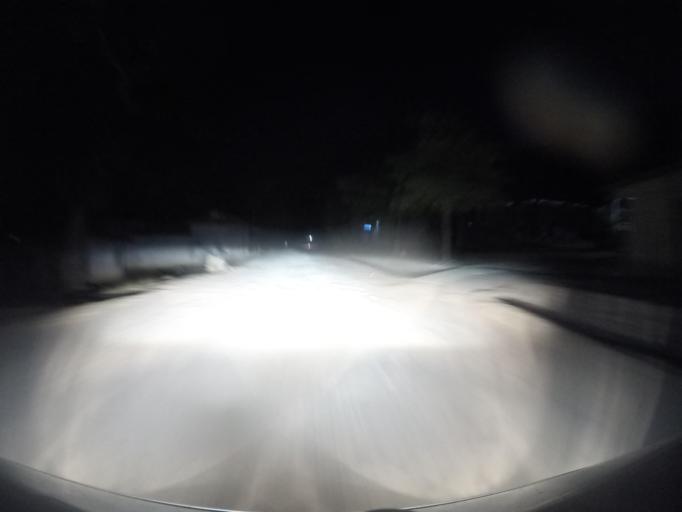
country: TL
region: Viqueque
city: Viqueque
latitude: -8.7977
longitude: 126.5553
